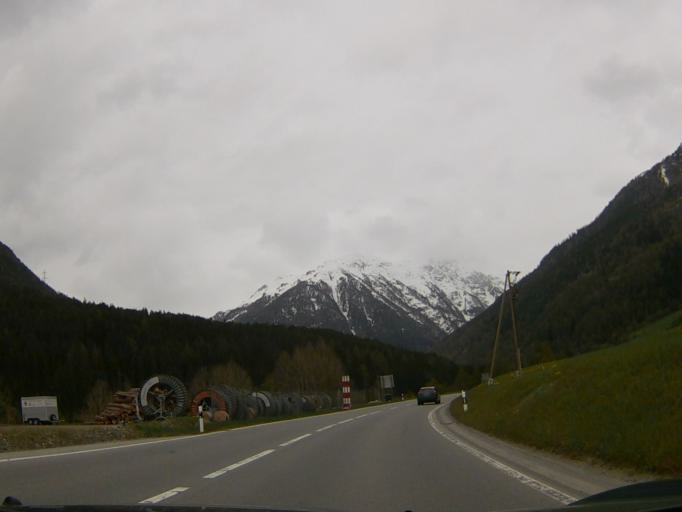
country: CH
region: Grisons
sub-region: Inn District
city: Zernez
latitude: 46.7638
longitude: 10.1062
